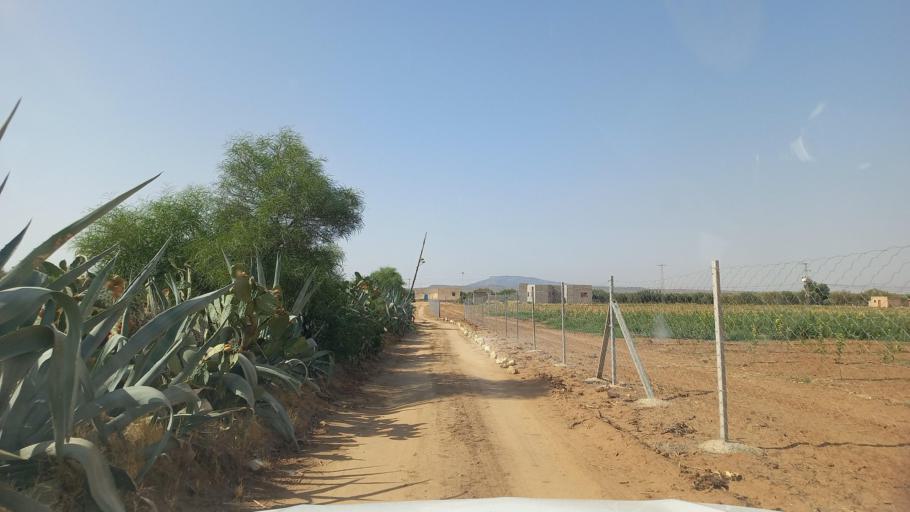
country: TN
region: Al Qasrayn
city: Kasserine
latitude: 35.2398
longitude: 9.0504
